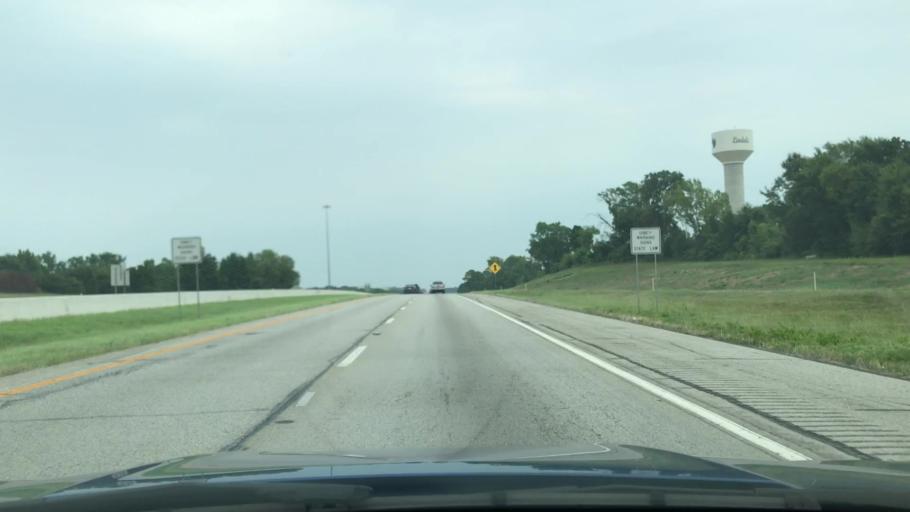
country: US
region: Texas
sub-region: Smith County
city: Hideaway
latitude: 32.4687
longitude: -95.4292
